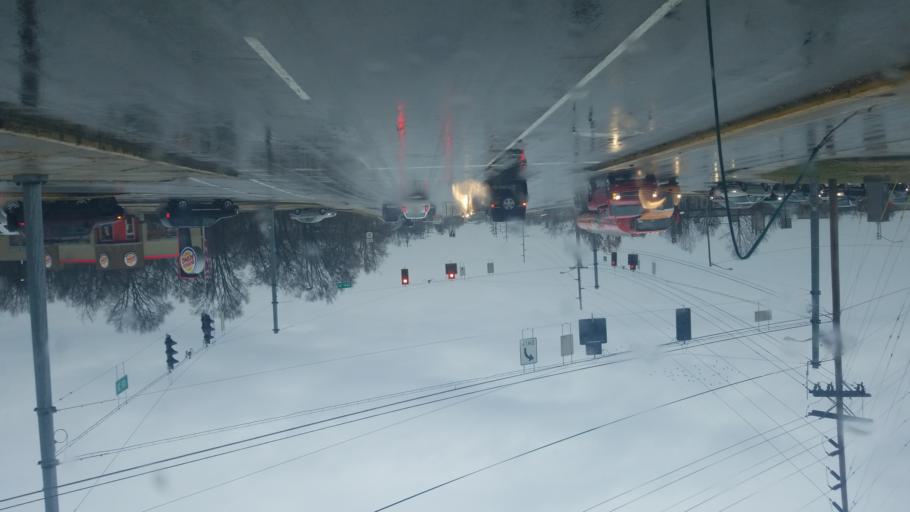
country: US
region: Indiana
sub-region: Bartholomew County
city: Columbus
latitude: 39.2229
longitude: -85.8907
